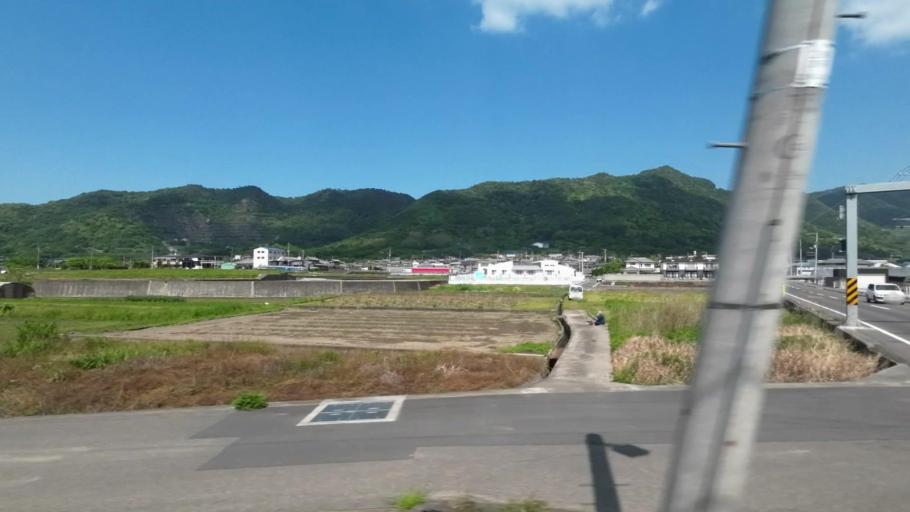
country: JP
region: Kagawa
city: Kan'onjicho
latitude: 34.1510
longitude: 133.6872
